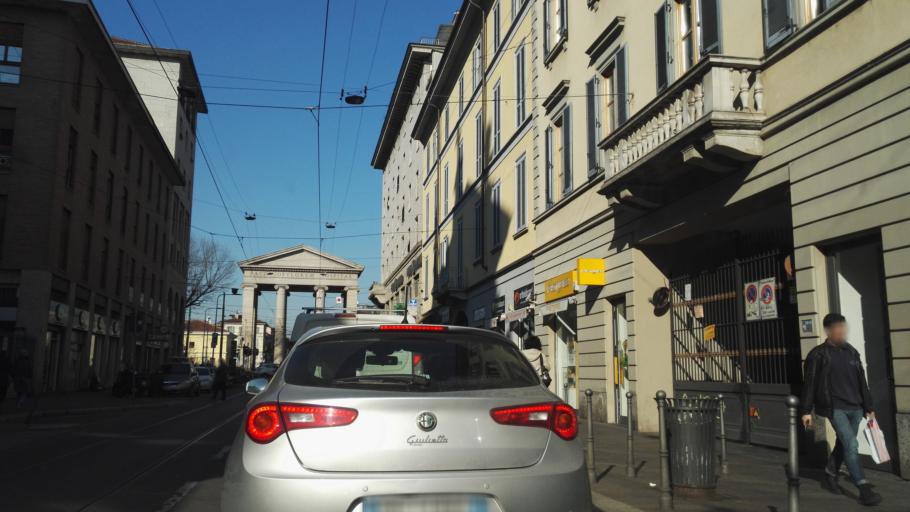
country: IT
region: Lombardy
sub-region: Citta metropolitana di Milano
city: Milano
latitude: 45.4512
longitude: 9.1800
